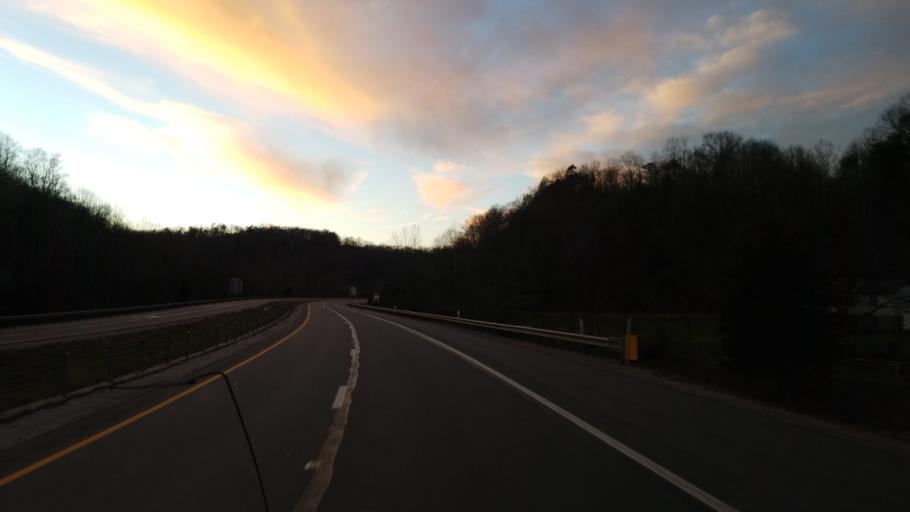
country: US
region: West Virginia
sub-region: Jackson County
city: Ripley
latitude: 38.7668
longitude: -81.7120
